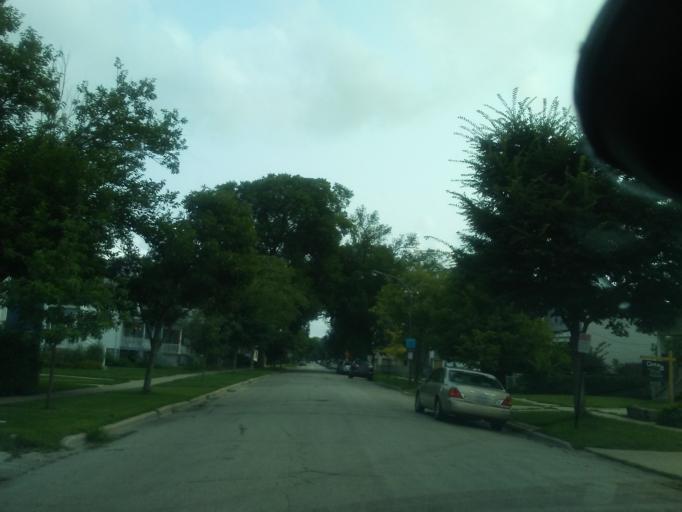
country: US
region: Illinois
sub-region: Cook County
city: Evanston
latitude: 42.0492
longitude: -87.6974
